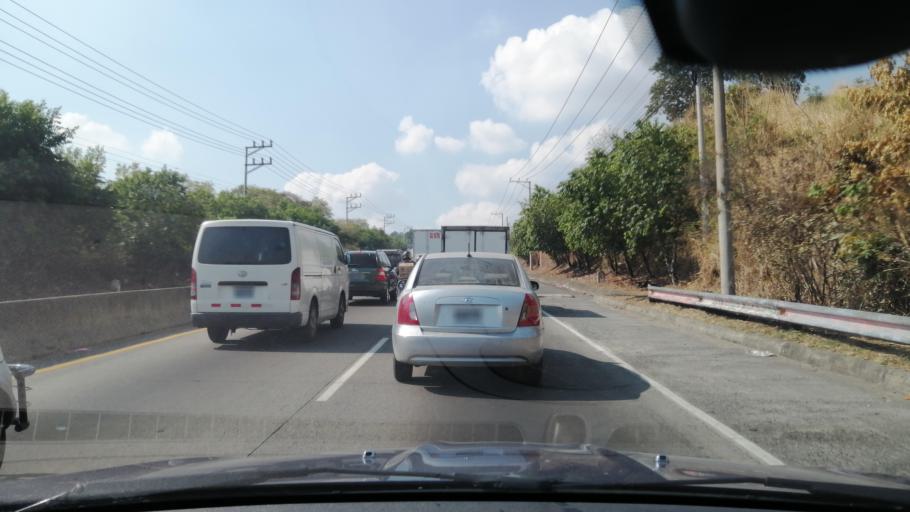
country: SV
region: San Salvador
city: Mejicanos
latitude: 13.7519
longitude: -89.2175
